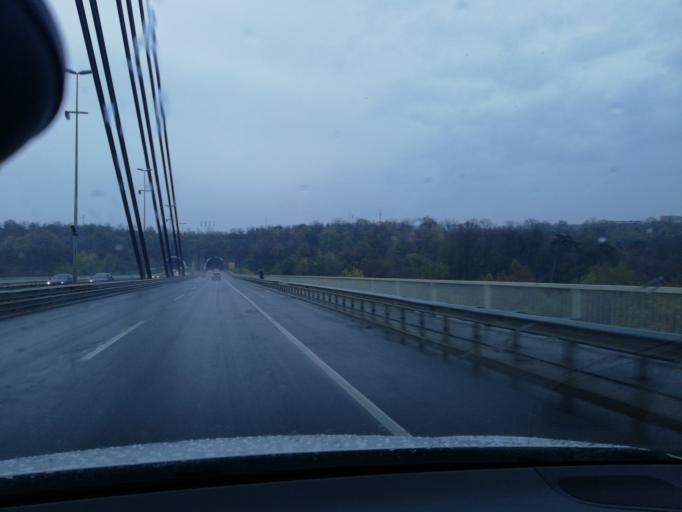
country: RS
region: Autonomna Pokrajina Vojvodina
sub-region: Juznobacki Okrug
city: Novi Sad
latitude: 45.2323
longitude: 19.8517
